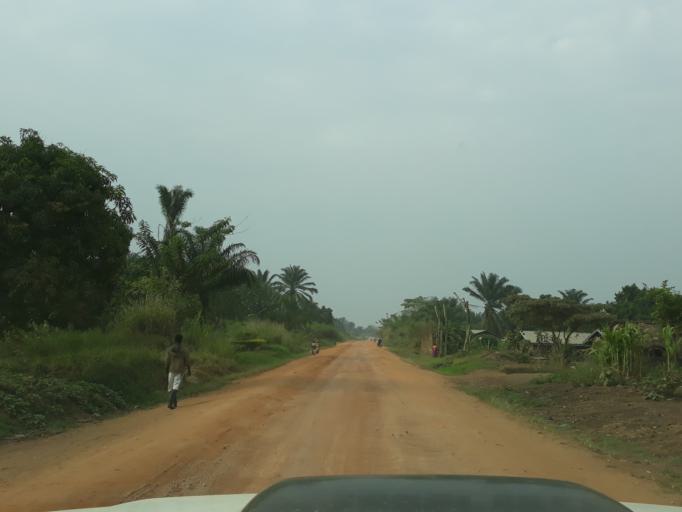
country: CD
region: Eastern Province
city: Bunia
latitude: 1.3432
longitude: 29.7550
